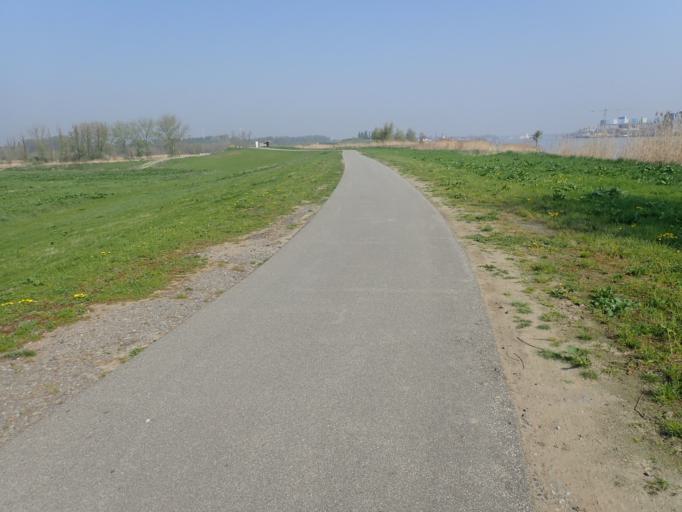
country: BE
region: Flanders
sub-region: Provincie Oost-Vlaanderen
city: Kruibeke
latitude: 51.1649
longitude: 4.3261
